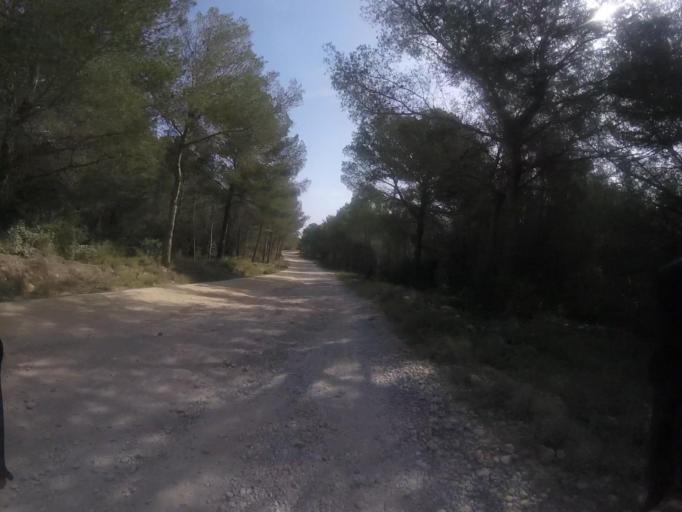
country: ES
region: Valencia
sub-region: Provincia de Castello
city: Alcoceber
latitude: 40.2732
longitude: 0.3090
